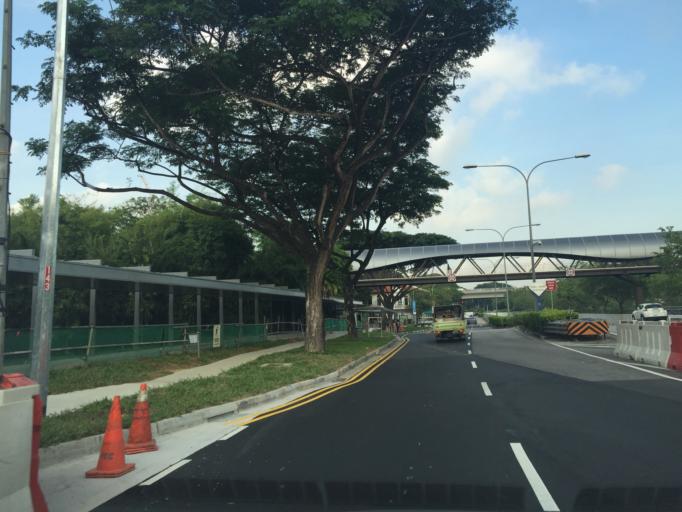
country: SG
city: Singapore
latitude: 1.3227
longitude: 103.8158
